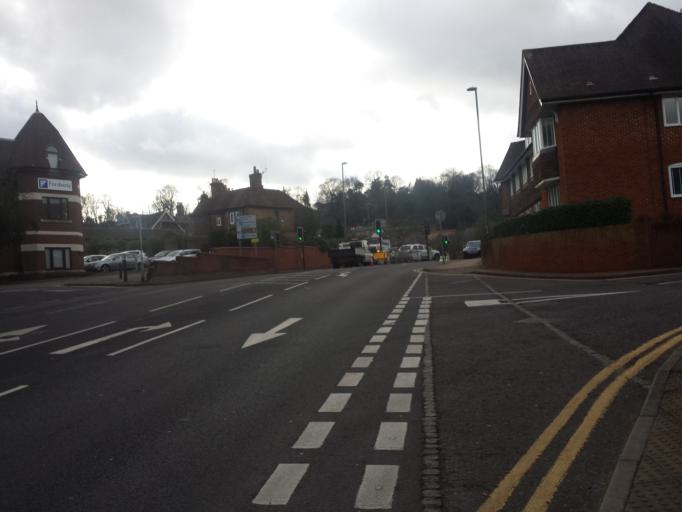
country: GB
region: England
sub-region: Surrey
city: Godalming
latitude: 51.1858
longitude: -0.6090
